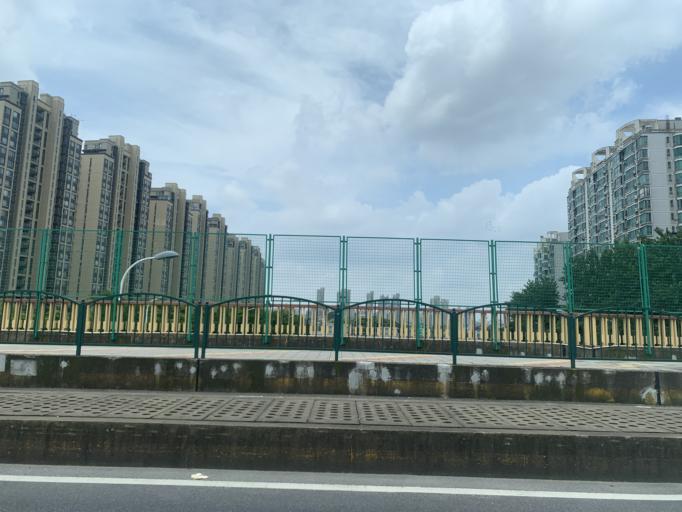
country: CN
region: Shanghai Shi
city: Huamu
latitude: 31.1994
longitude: 121.5338
